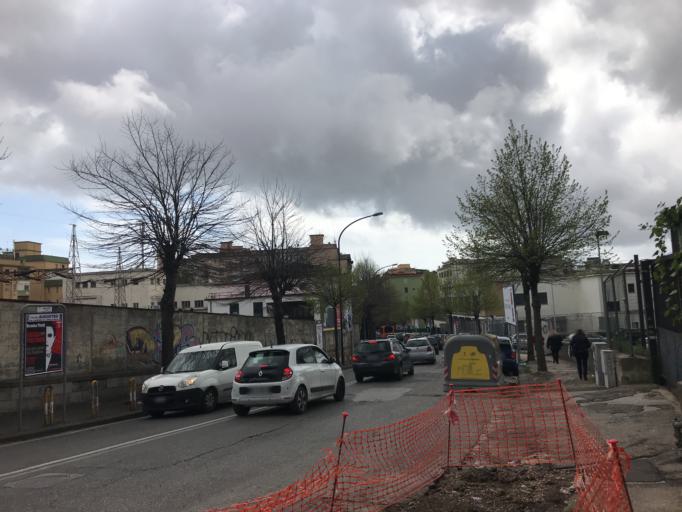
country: IT
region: Campania
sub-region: Provincia di Napoli
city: Napoli
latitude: 40.8564
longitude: 14.2247
